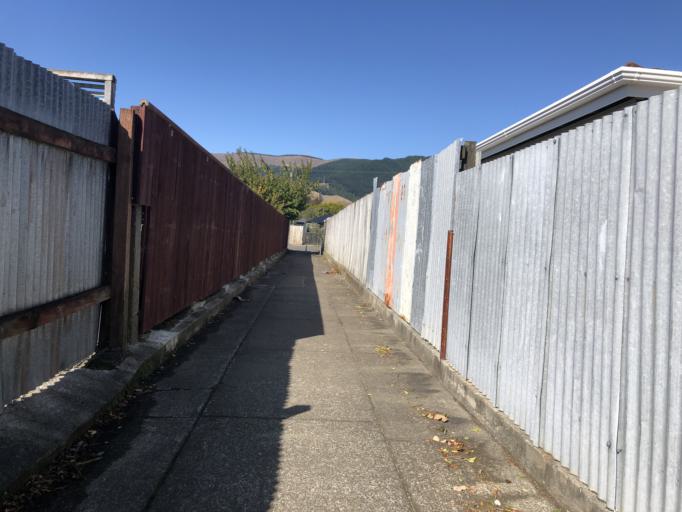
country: NZ
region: Tasman
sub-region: Tasman District
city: Richmond
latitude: -41.3401
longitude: 173.1773
